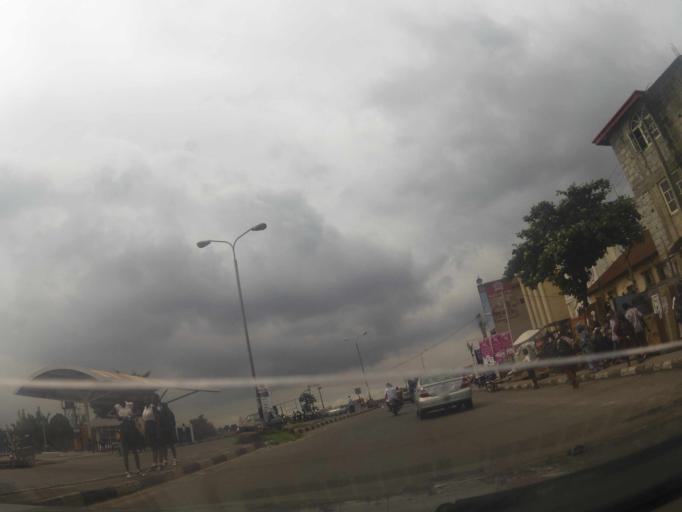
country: NG
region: Oyo
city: Ibadan
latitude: 7.4066
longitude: 3.8894
